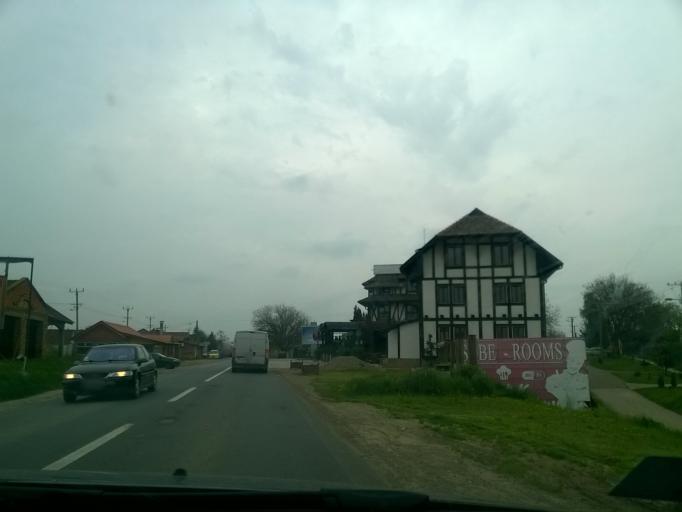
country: RS
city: Platicevo
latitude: 44.8261
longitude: 19.7795
